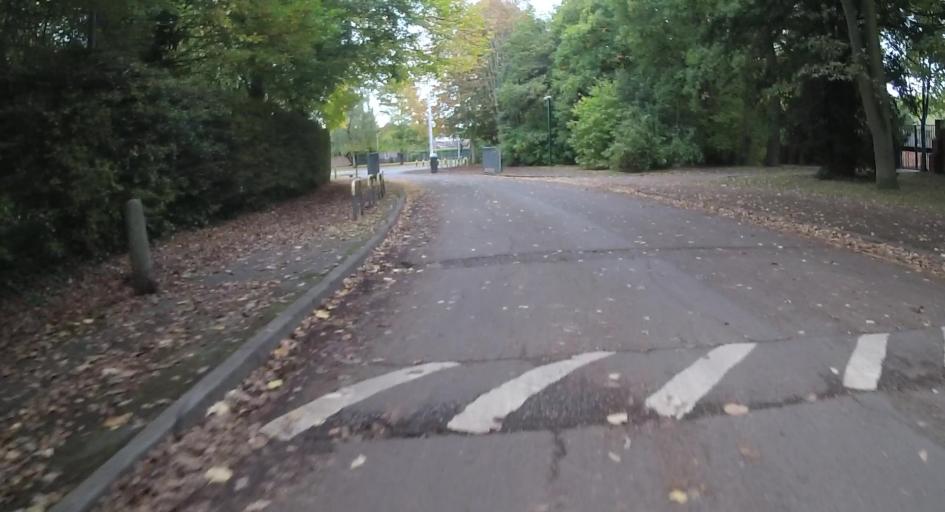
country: GB
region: England
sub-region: Bracknell Forest
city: Crowthorne
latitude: 51.3988
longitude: -0.7819
